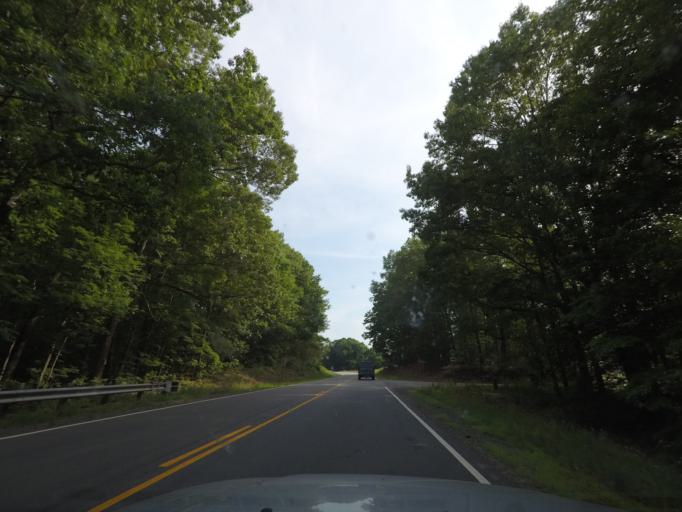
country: US
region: Virginia
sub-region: Mecklenburg County
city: Chase City
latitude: 36.8045
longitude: -78.6031
